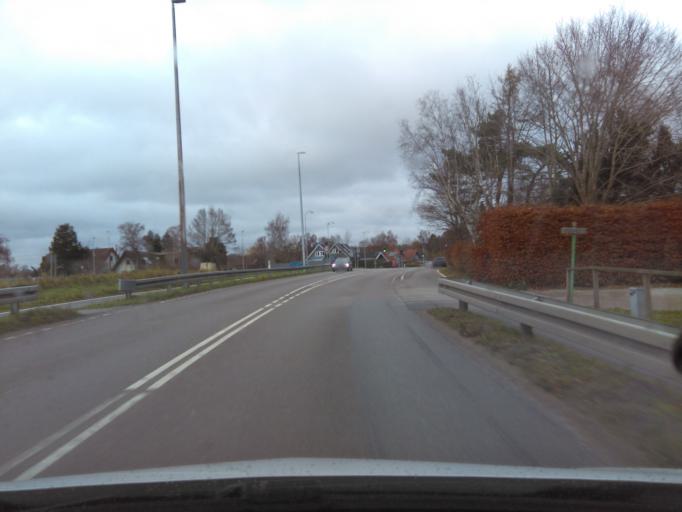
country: DK
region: Capital Region
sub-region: Fureso Kommune
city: Vaerlose
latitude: 55.7645
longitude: 12.3661
